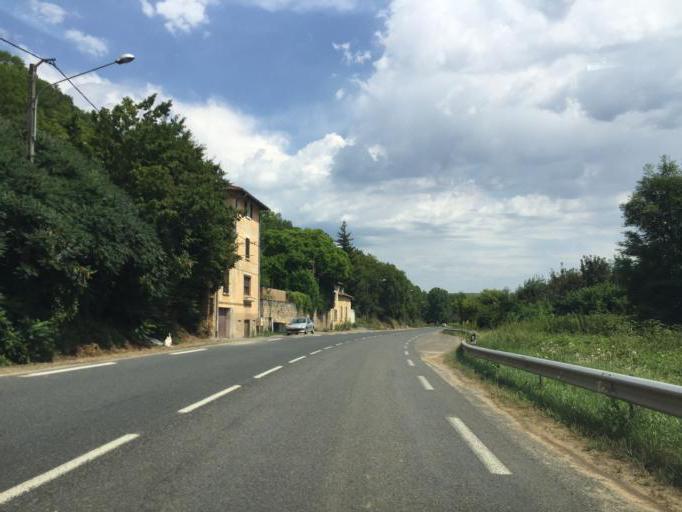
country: FR
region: Rhone-Alpes
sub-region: Departement du Rhone
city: Saint-Germain-Nuelles
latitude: 45.8409
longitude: 4.5991
